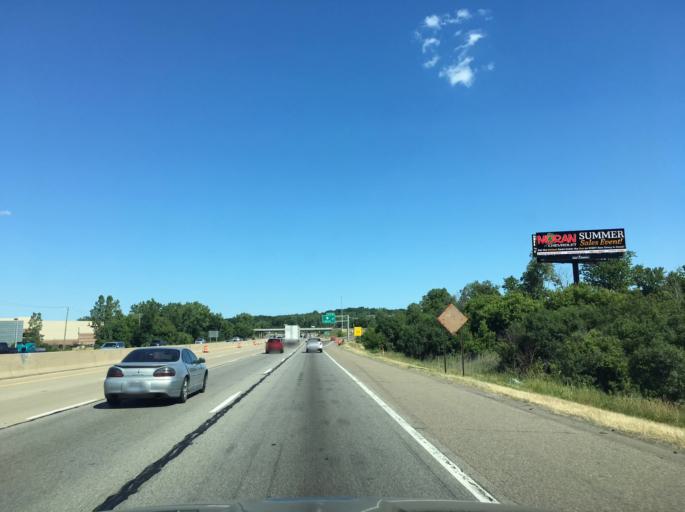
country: US
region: Michigan
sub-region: Oakland County
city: Auburn Hills
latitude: 42.6886
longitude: -83.2478
